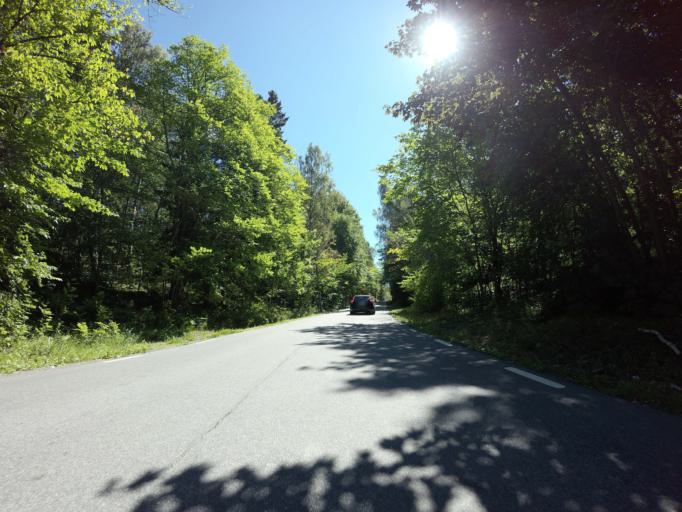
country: SE
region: Stockholm
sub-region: Lidingo
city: Lidingoe
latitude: 59.3384
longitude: 18.1319
